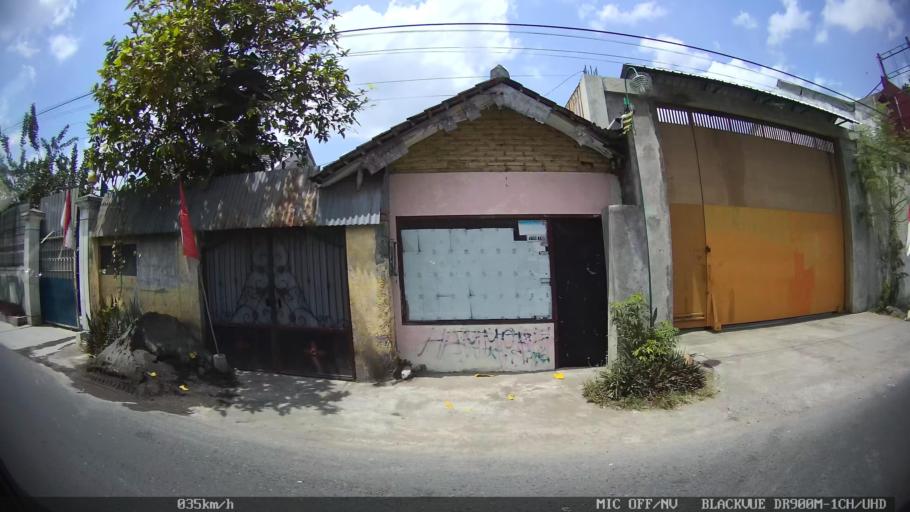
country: ID
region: Daerah Istimewa Yogyakarta
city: Gamping Lor
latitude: -7.8038
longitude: 110.3414
